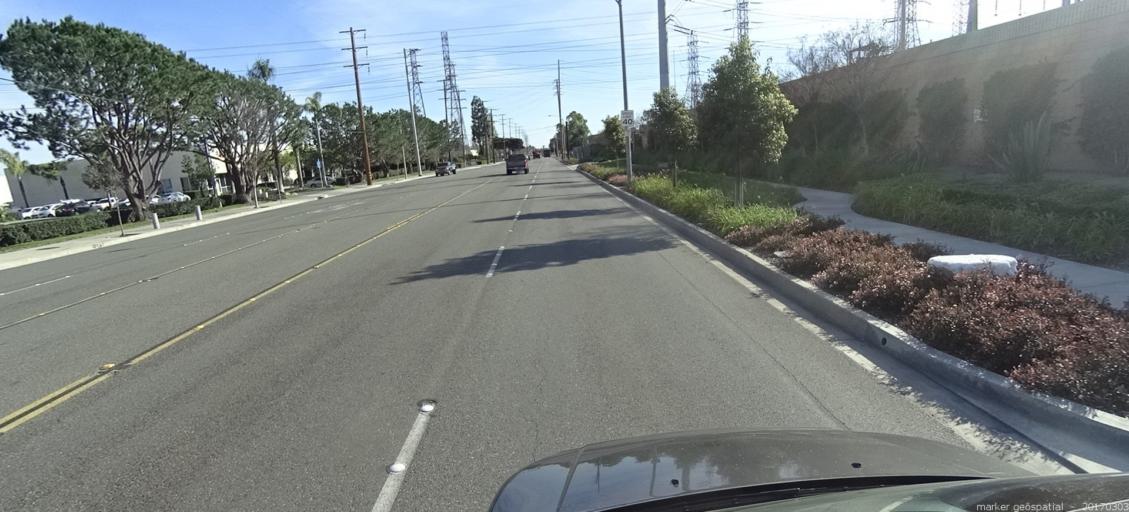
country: US
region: California
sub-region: Orange County
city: Anaheim
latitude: 33.8100
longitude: -117.8980
